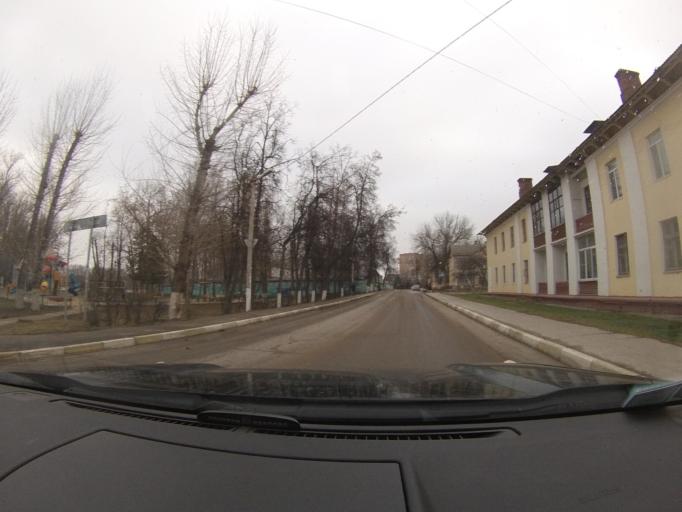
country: RU
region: Moskovskaya
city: Peski
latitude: 55.2498
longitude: 38.7615
